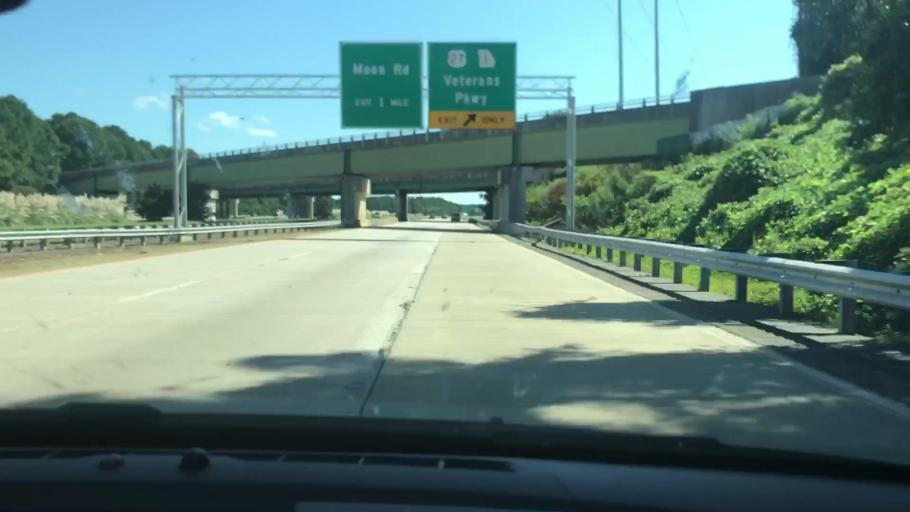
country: US
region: Alabama
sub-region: Russell County
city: Phenix City
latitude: 32.5474
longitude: -84.9529
